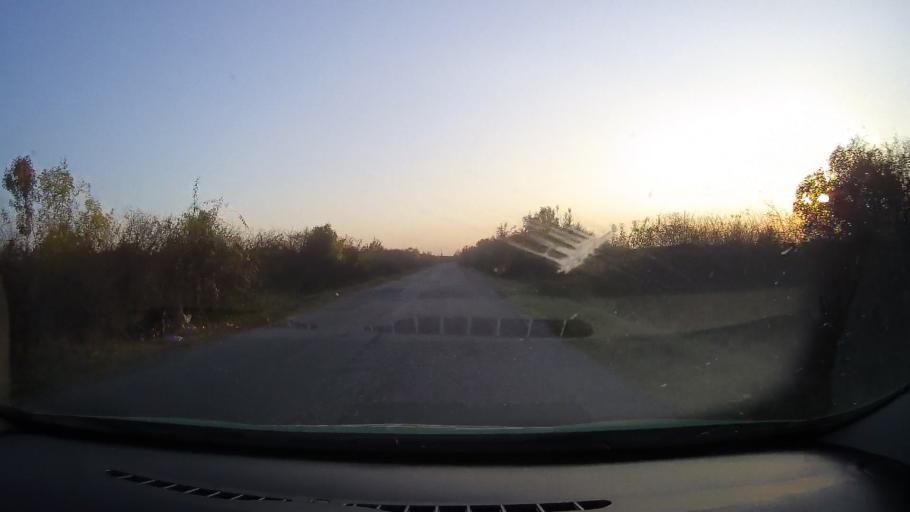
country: RO
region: Arad
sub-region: Comuna Seleus
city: Seleus
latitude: 46.4061
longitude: 21.7295
